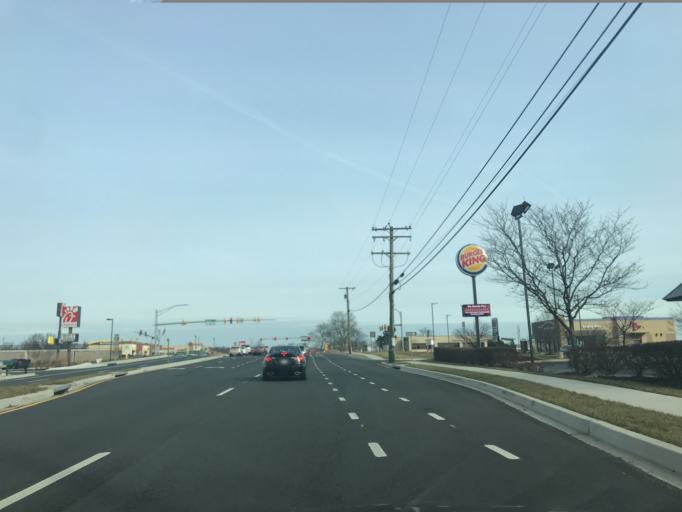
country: US
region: Maryland
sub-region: Harford County
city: Aberdeen
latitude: 39.5216
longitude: -76.1847
